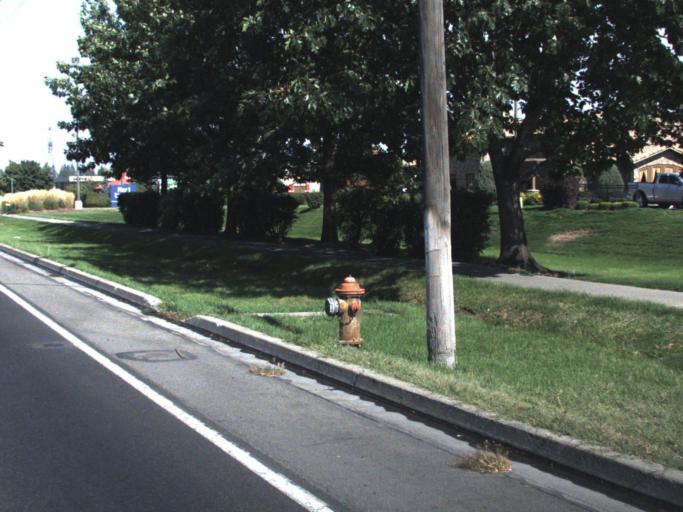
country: US
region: Washington
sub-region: Spokane County
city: Country Homes
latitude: 47.7489
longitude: -117.4024
